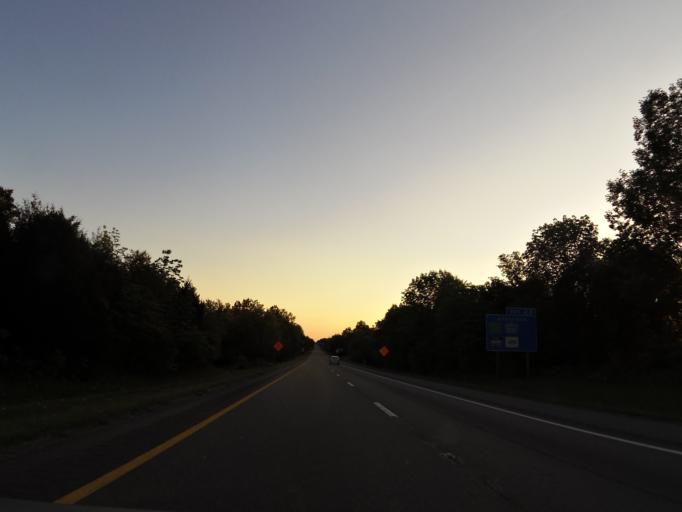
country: US
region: Tennessee
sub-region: Greene County
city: Mosheim
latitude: 36.2353
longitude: -83.0098
